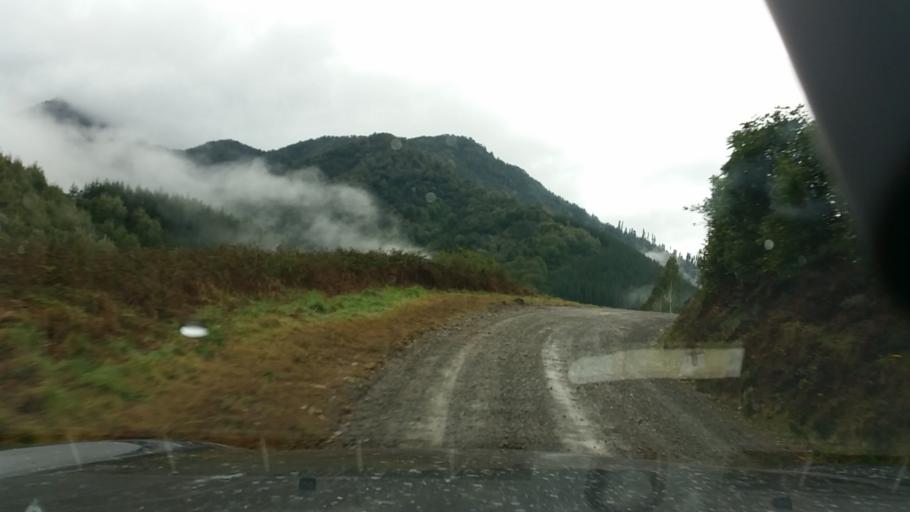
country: NZ
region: Nelson
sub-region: Nelson City
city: Nelson
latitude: -41.3629
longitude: 173.6055
